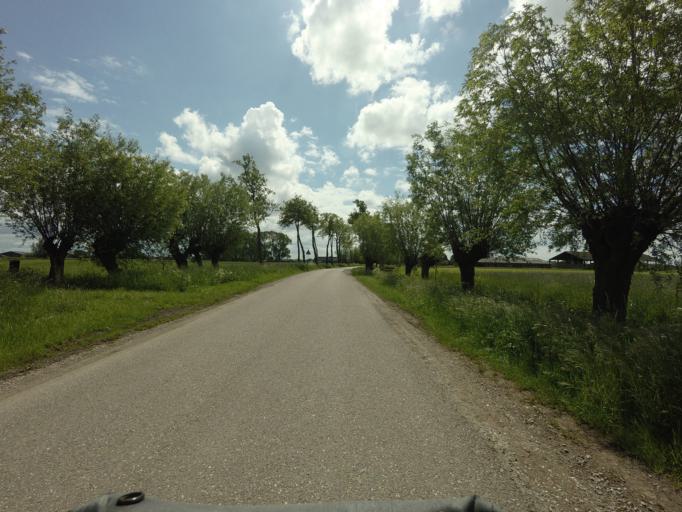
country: NL
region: South Holland
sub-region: Gemeente Gorinchem
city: Gorinchem
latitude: 51.8636
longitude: 4.9383
